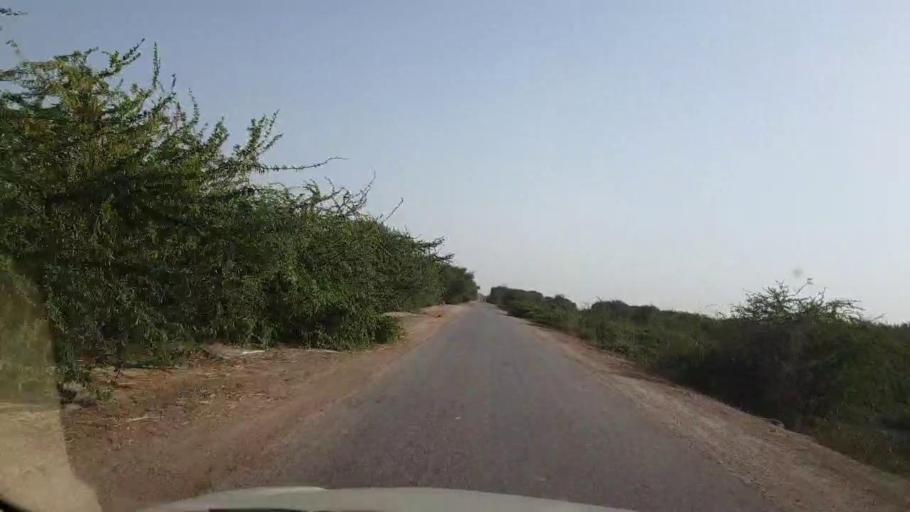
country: PK
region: Sindh
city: Tando Ghulam Ali
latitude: 25.0988
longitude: 68.8689
